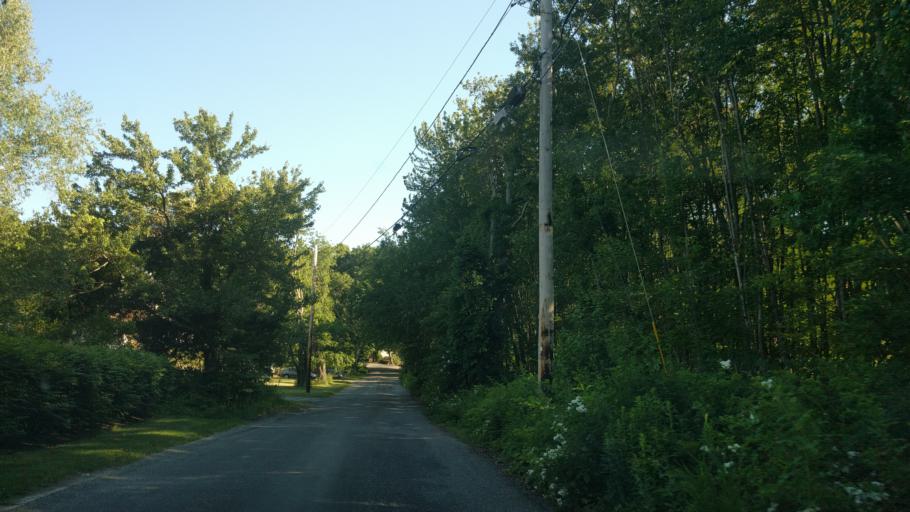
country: US
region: Massachusetts
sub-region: Worcester County
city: Oxford
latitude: 42.1409
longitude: -71.8362
